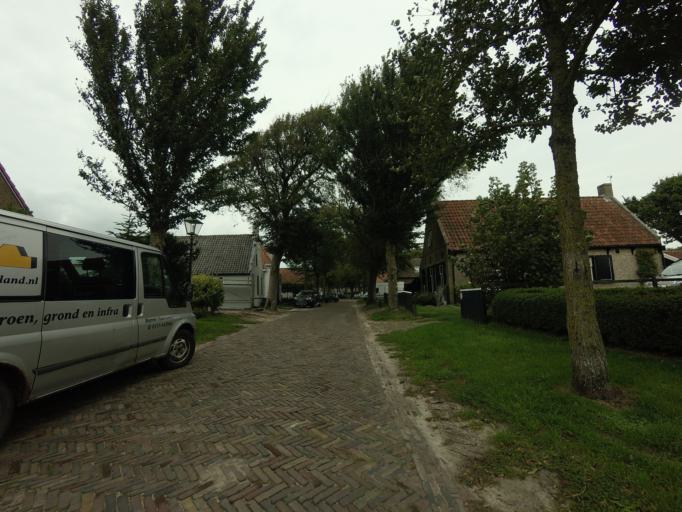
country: NL
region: Friesland
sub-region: Gemeente Ameland
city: Hollum
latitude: 53.4347
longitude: 5.6403
